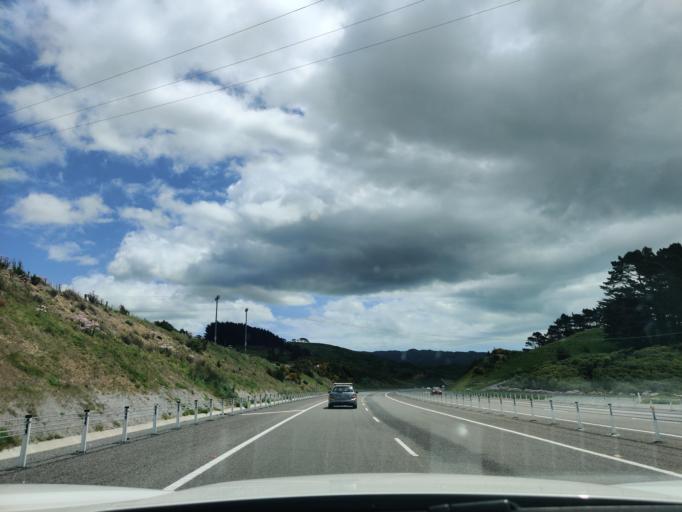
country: NZ
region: Wellington
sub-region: Porirua City
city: Porirua
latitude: -41.1558
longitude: 174.8715
